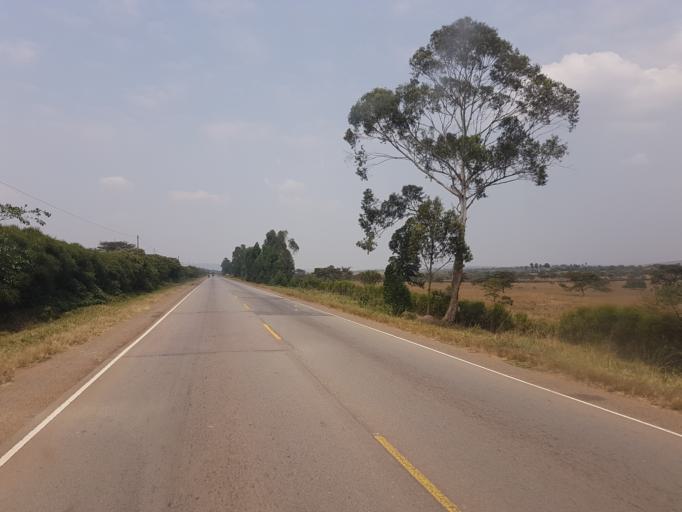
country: UG
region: Western Region
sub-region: Mbarara District
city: Mbarara
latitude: -0.5106
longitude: 30.7837
